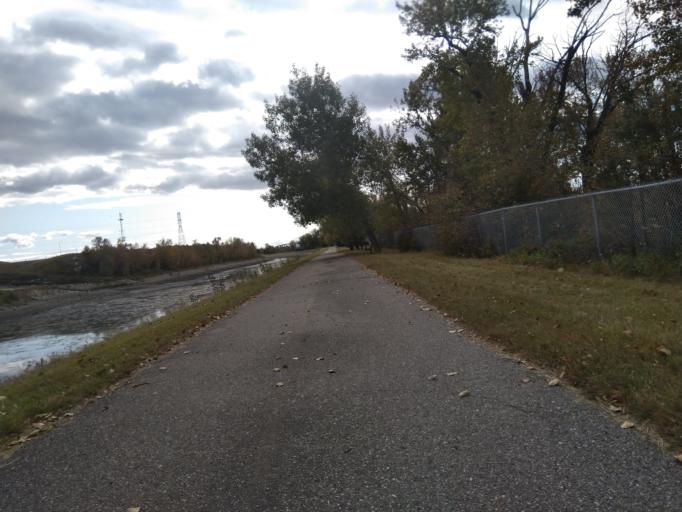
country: CA
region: Alberta
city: Calgary
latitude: 51.0206
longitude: -114.0066
